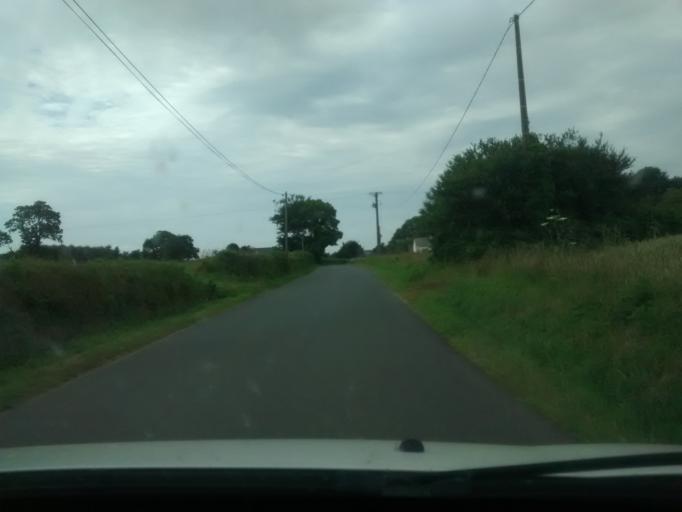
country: FR
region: Brittany
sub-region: Departement des Cotes-d'Armor
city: Trelevern
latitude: 48.7989
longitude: -3.3640
